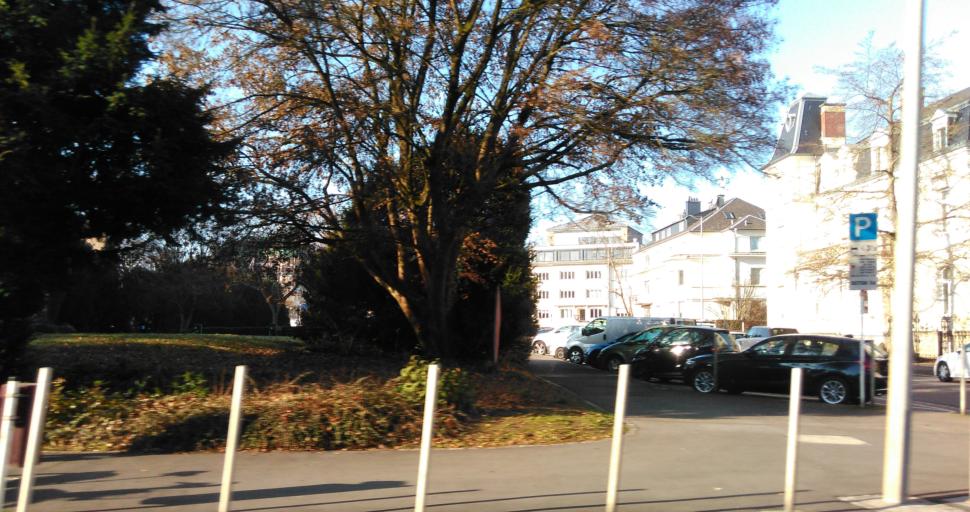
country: LU
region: Luxembourg
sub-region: Canton de Luxembourg
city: Luxembourg
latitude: 49.6115
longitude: 6.1201
